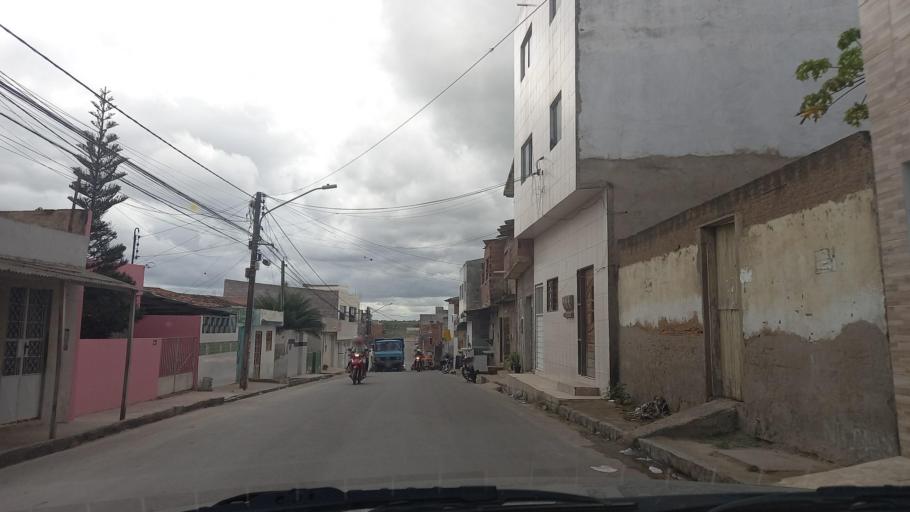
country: BR
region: Pernambuco
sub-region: Caruaru
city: Caruaru
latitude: -8.2645
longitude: -35.9568
